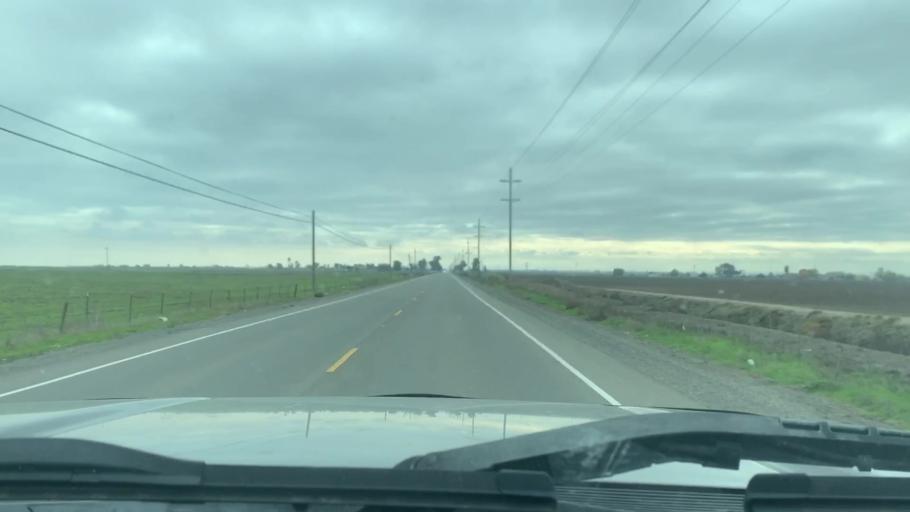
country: US
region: California
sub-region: Merced County
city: Los Banos
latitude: 37.1118
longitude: -120.8349
